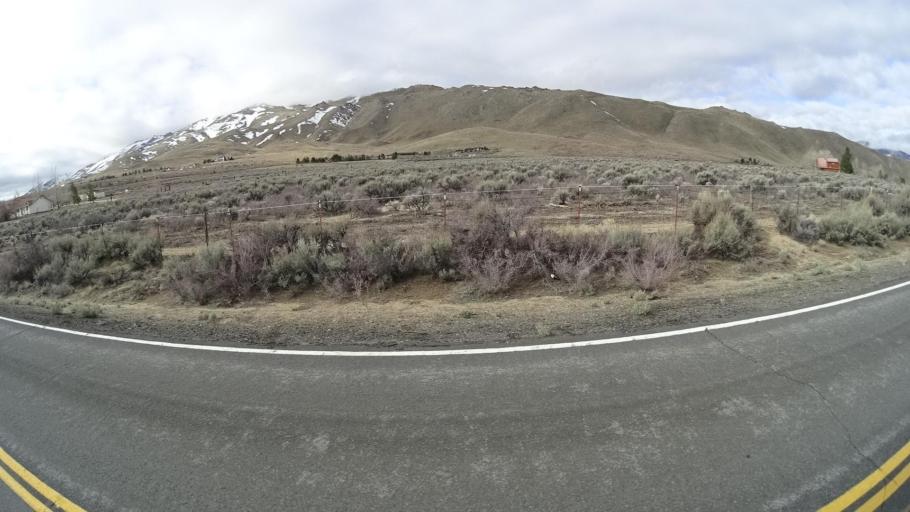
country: US
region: Nevada
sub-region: Washoe County
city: Cold Springs
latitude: 39.8882
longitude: -119.9734
